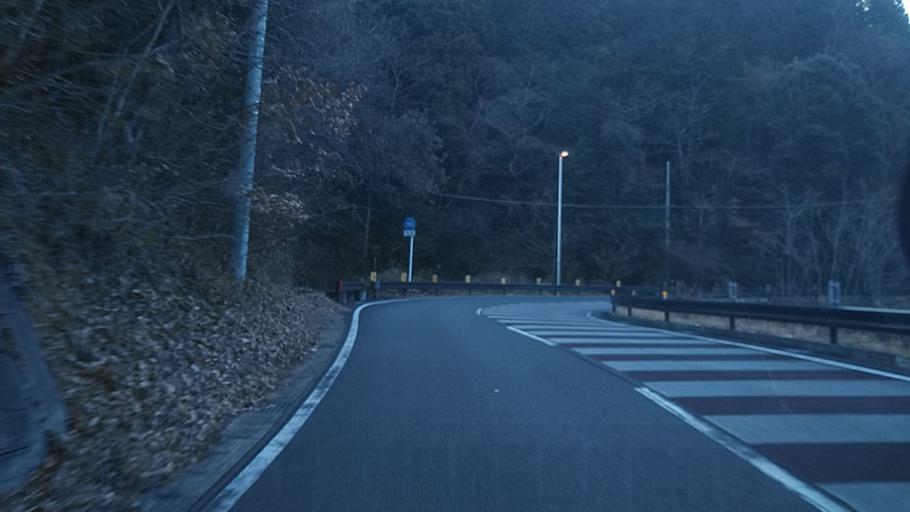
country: JP
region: Chiba
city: Kimitsu
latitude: 35.2638
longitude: 139.9314
